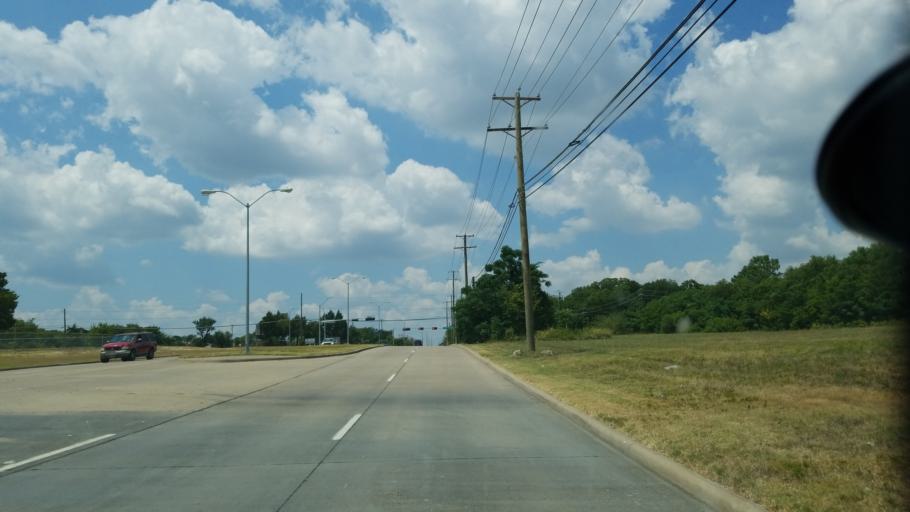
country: US
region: Texas
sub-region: Dallas County
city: Duncanville
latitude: 32.6767
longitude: -96.8896
